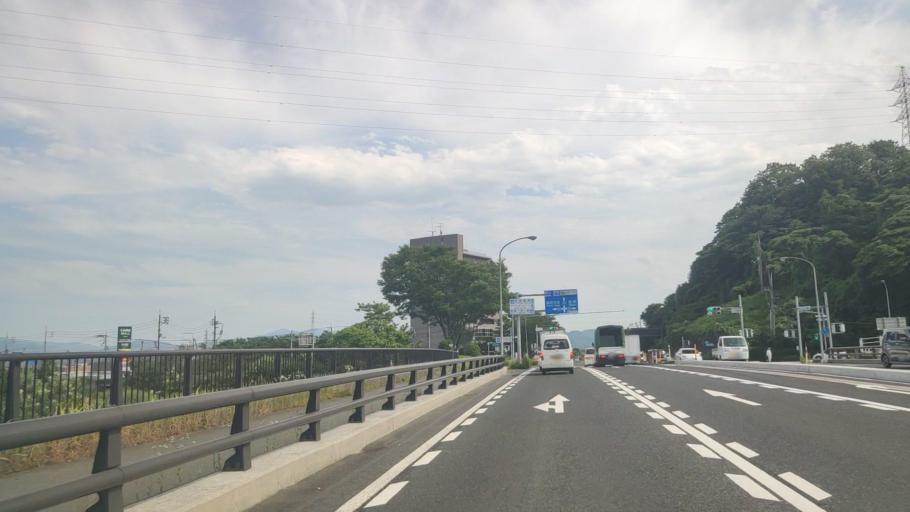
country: JP
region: Tottori
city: Tottori
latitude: 35.4995
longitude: 134.2019
